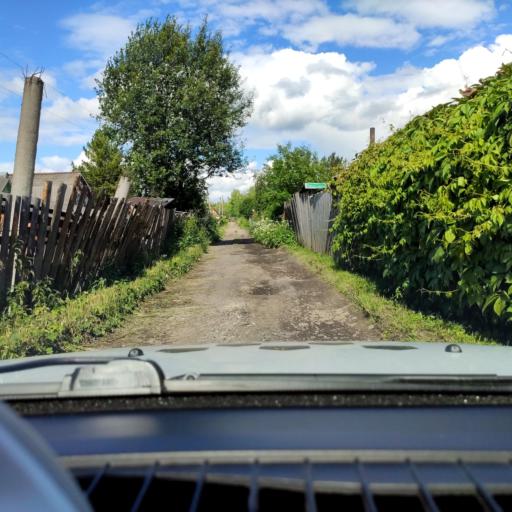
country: RU
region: Perm
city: Overyata
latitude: 58.1025
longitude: 55.8640
